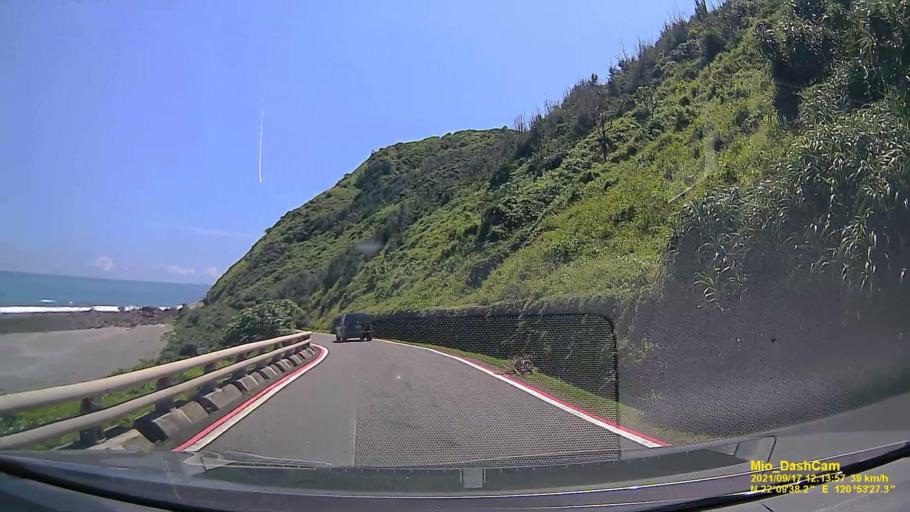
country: TW
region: Taiwan
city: Hengchun
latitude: 22.1605
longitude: 120.8910
